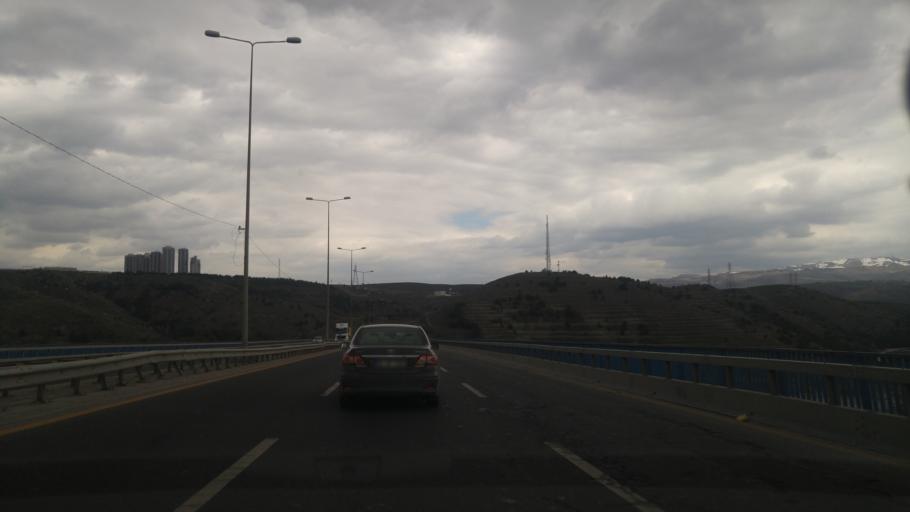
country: TR
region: Ankara
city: Mamak
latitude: 39.8896
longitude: 32.9056
